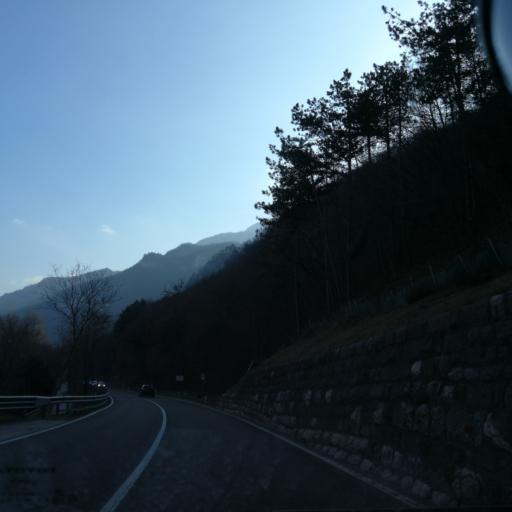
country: IT
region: Trentino-Alto Adige
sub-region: Provincia di Trento
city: Nago-Torbole
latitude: 45.8621
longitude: 10.9172
